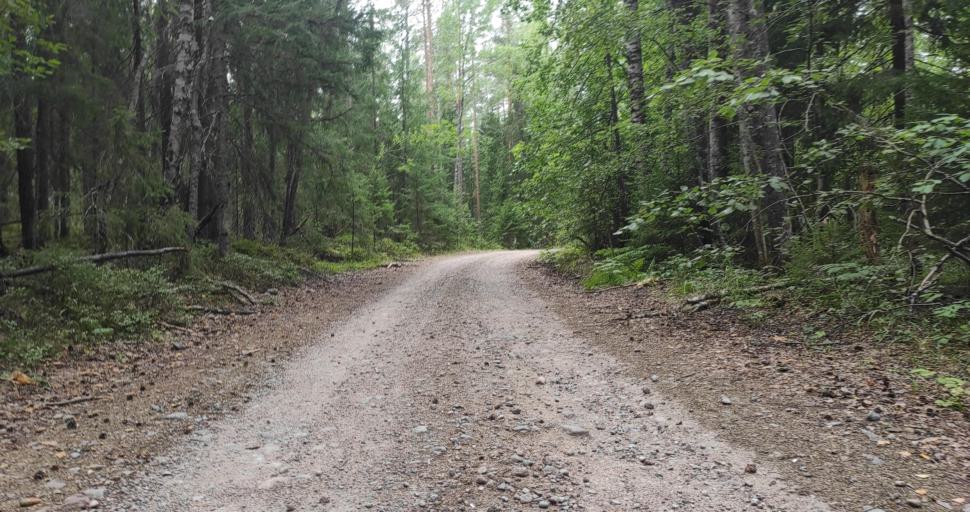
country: RU
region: Leningrad
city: Veshchevo
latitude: 60.6863
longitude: 29.2447
